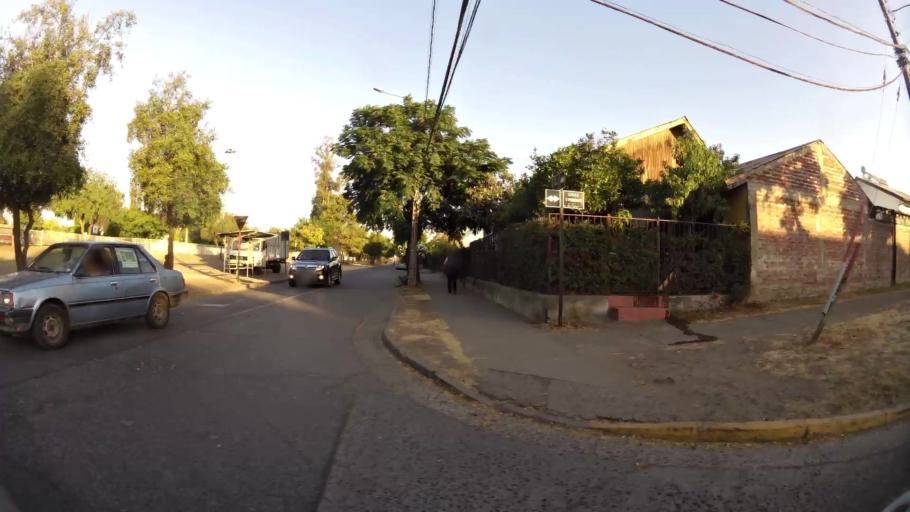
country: CL
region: Maule
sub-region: Provincia de Talca
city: Talca
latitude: -35.4407
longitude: -71.6777
